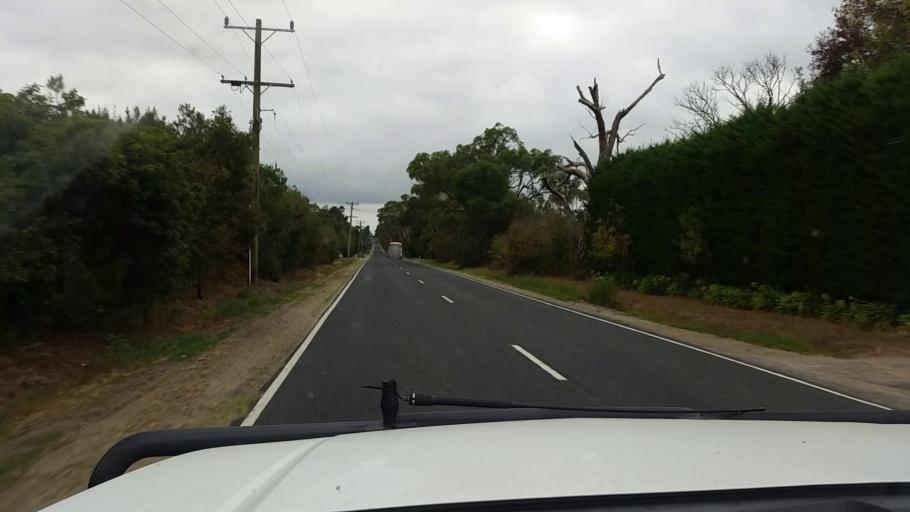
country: AU
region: Victoria
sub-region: Mornington Peninsula
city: Tyabb
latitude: -38.2728
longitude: 145.1456
